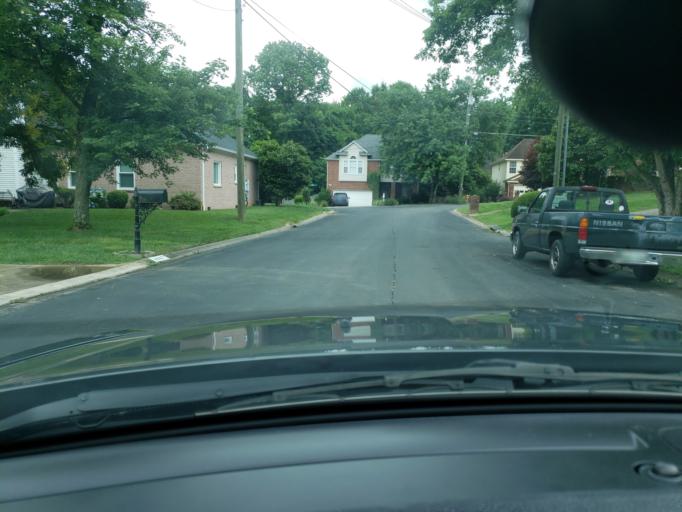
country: US
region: Tennessee
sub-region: Williamson County
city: Nolensville
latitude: 36.0362
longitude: -86.6784
